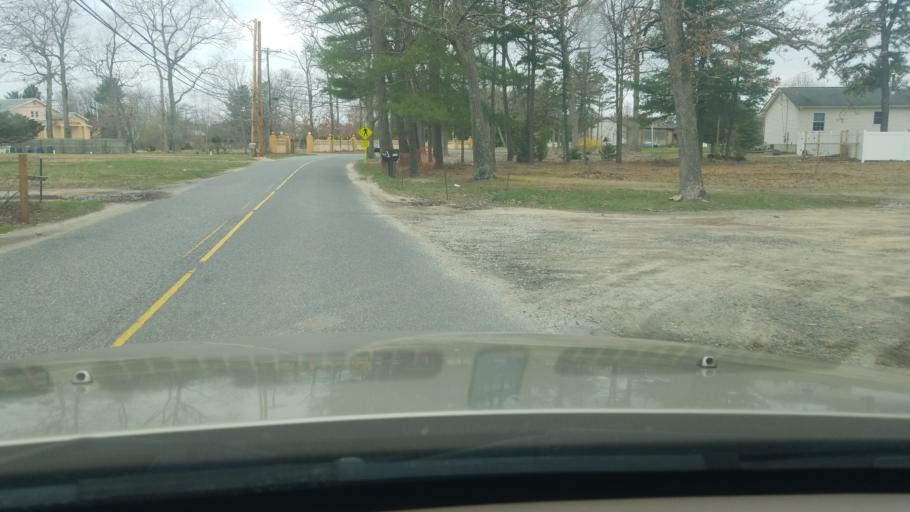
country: US
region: New Jersey
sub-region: Ocean County
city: Lakewood
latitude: 40.1144
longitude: -74.2147
